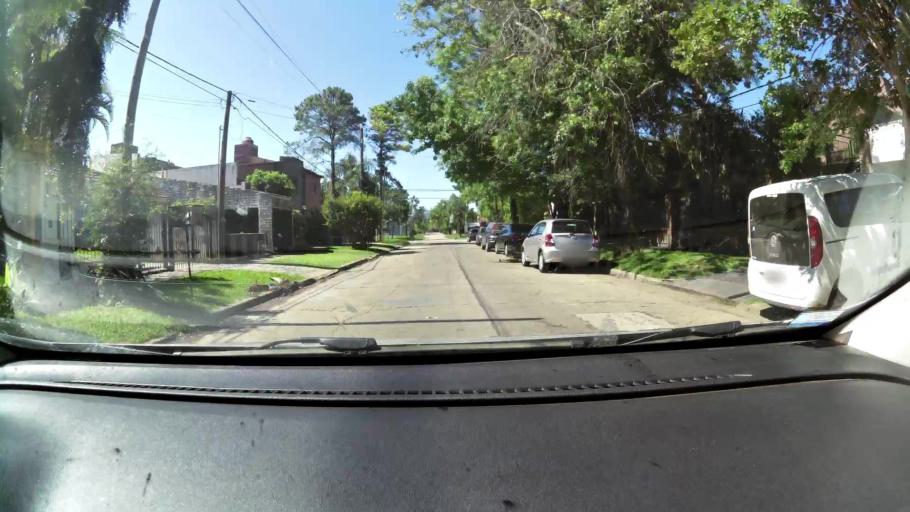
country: AR
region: Santa Fe
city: Santa Fe de la Vera Cruz
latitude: -31.5999
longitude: -60.6701
